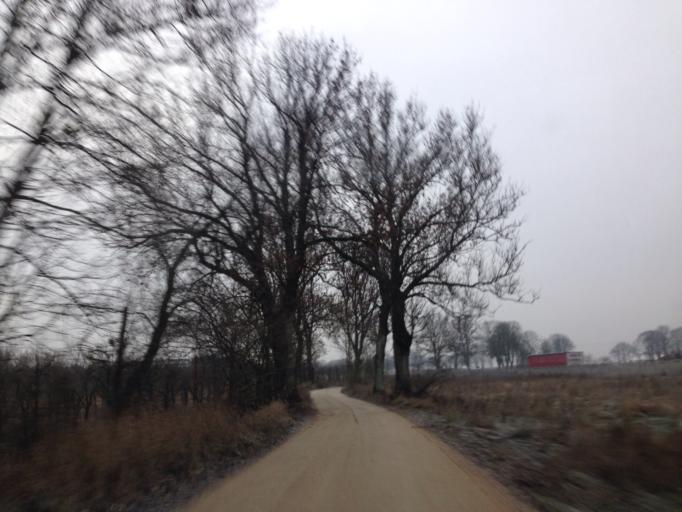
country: PL
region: Kujawsko-Pomorskie
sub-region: Powiat brodnicki
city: Gorzno
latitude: 53.2157
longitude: 19.6397
